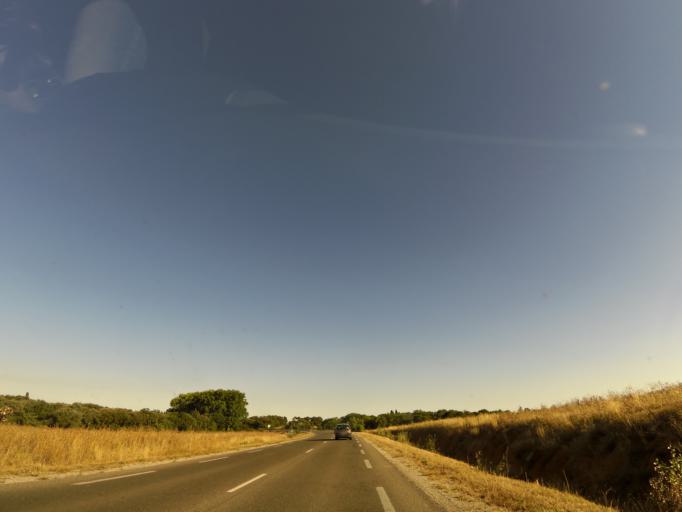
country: FR
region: Languedoc-Roussillon
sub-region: Departement du Gard
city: Sommieres
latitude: 43.8060
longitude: 4.0674
